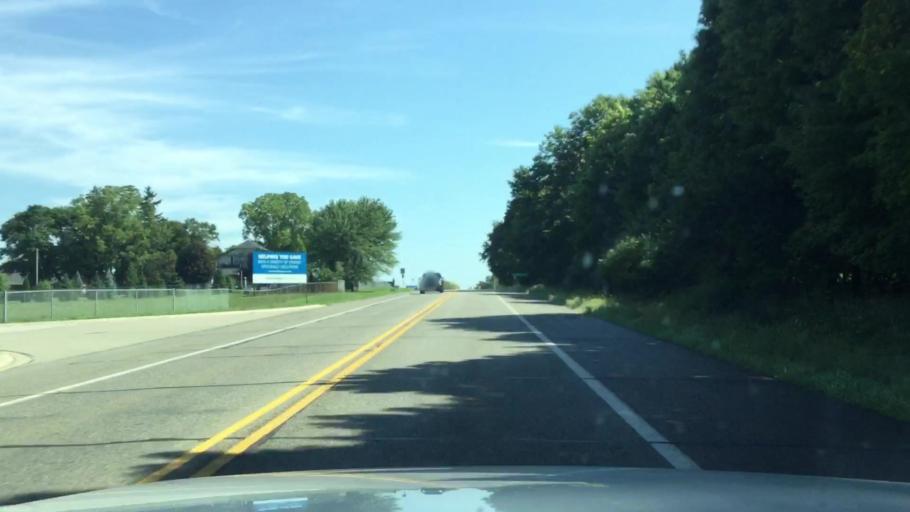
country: US
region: Michigan
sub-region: Jackson County
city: Brooklyn
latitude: 42.0572
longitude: -84.2518
